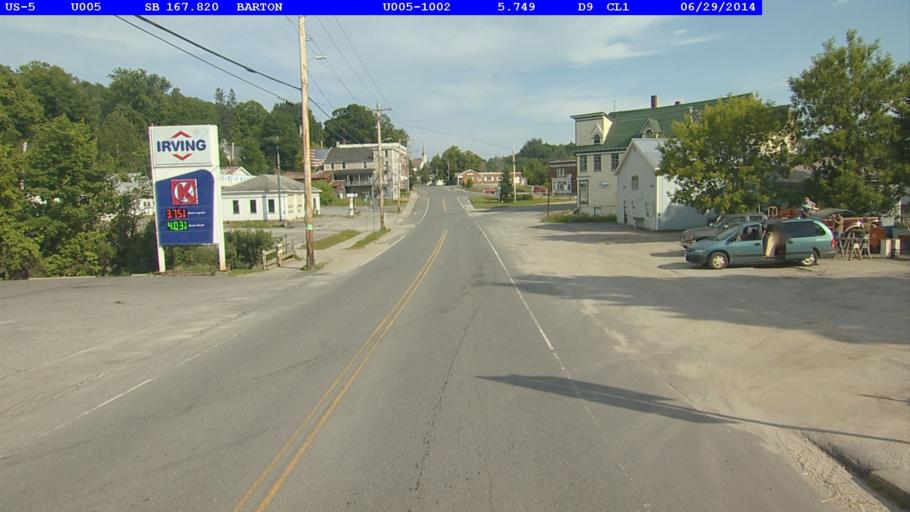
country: US
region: Vermont
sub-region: Orleans County
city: Newport
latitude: 44.7516
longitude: -72.1808
